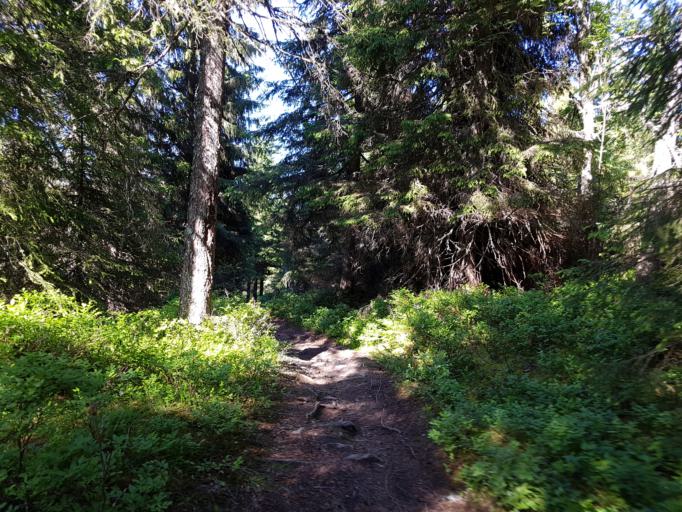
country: NO
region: Sor-Trondelag
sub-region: Trondheim
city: Trondheim
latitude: 63.4136
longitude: 10.3102
